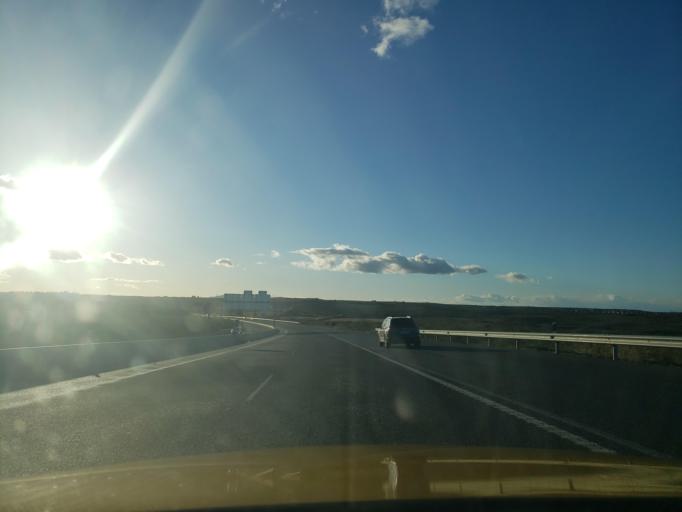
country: ES
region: Castille-La Mancha
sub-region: Province of Toledo
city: Burguillos de Toledo
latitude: 39.8157
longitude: -3.9888
